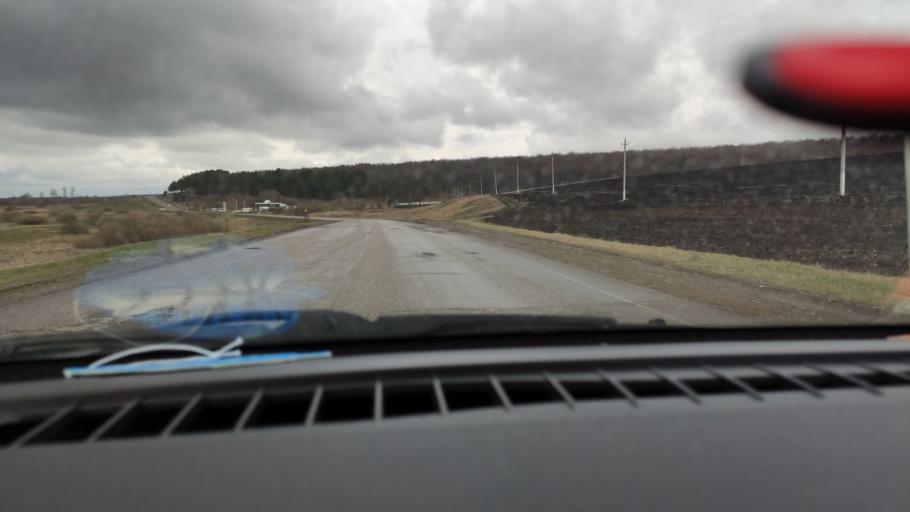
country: RU
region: Tatarstan
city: Nurlat
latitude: 54.3873
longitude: 50.7489
